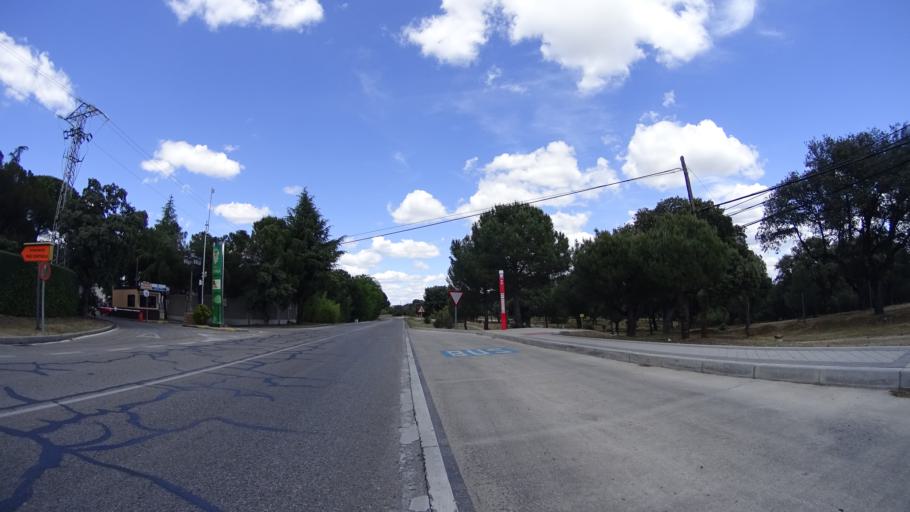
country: ES
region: Madrid
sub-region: Provincia de Madrid
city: Boadilla del Monte
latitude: 40.4206
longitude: -3.8751
